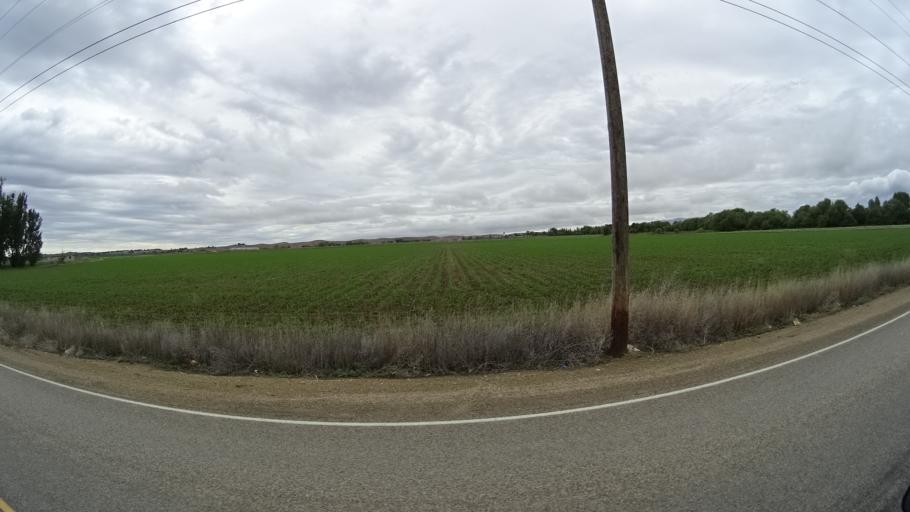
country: US
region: Idaho
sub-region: Ada County
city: Star
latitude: 43.7075
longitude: -116.4375
